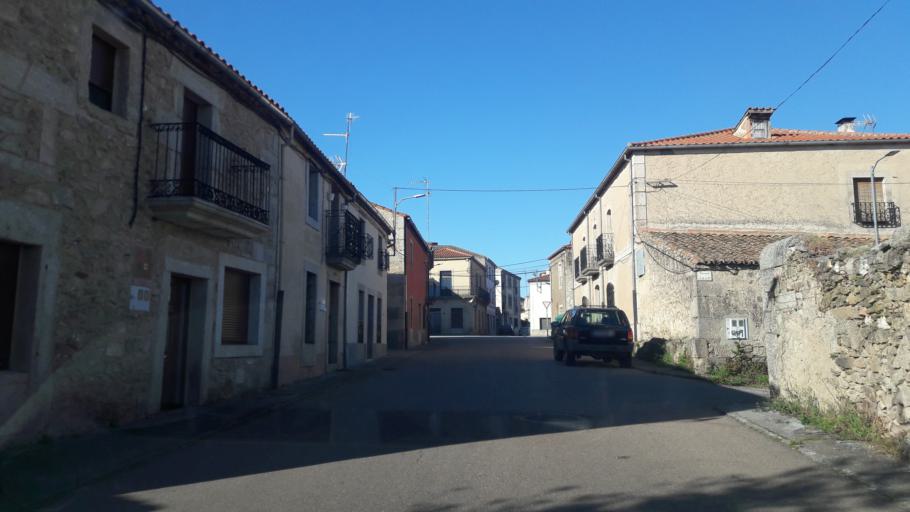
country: ES
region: Castille and Leon
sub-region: Provincia de Salamanca
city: Villavieja de Yeltes
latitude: 40.8772
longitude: -6.4679
